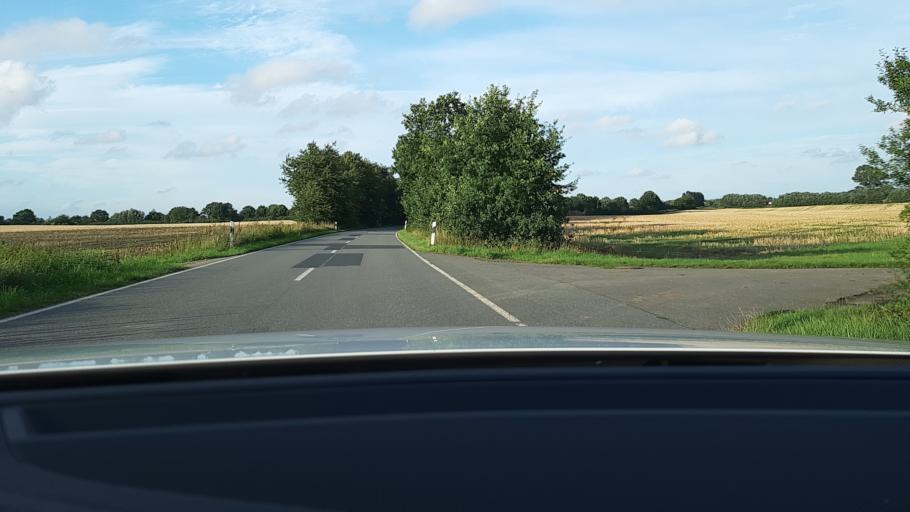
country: DE
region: Schleswig-Holstein
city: Monkhagen
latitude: 53.9311
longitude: 10.5826
